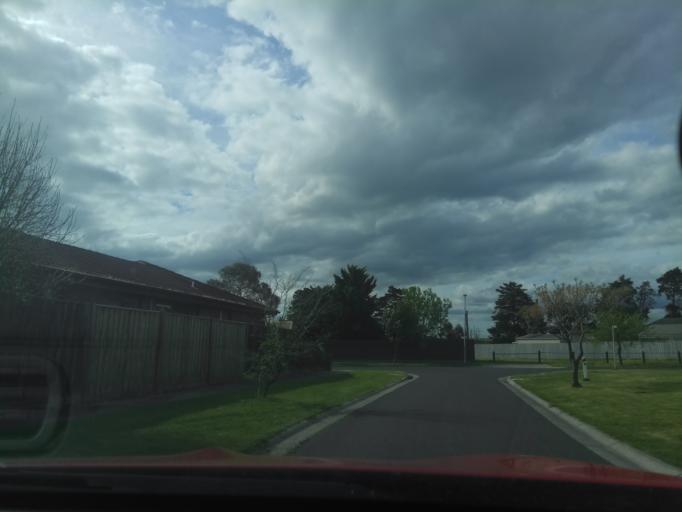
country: AU
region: Victoria
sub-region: Casey
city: Cranbourne North
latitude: -38.0680
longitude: 145.2756
